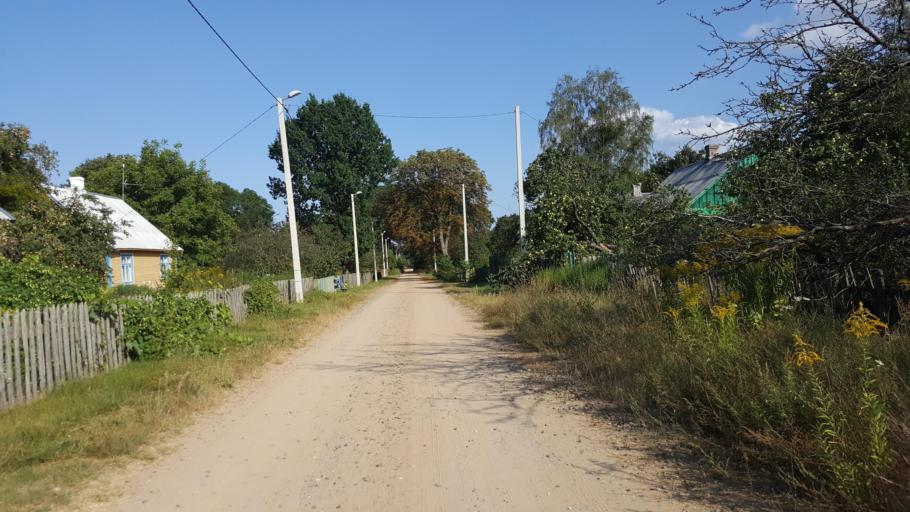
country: BY
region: Brest
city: Kamyanyuki
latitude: 52.5618
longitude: 23.6358
